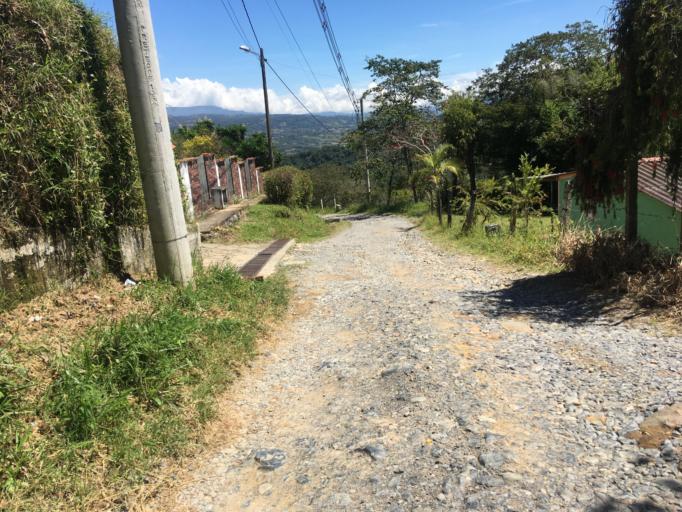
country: CO
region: Santander
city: Barbosa
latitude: 5.9150
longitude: -73.5984
